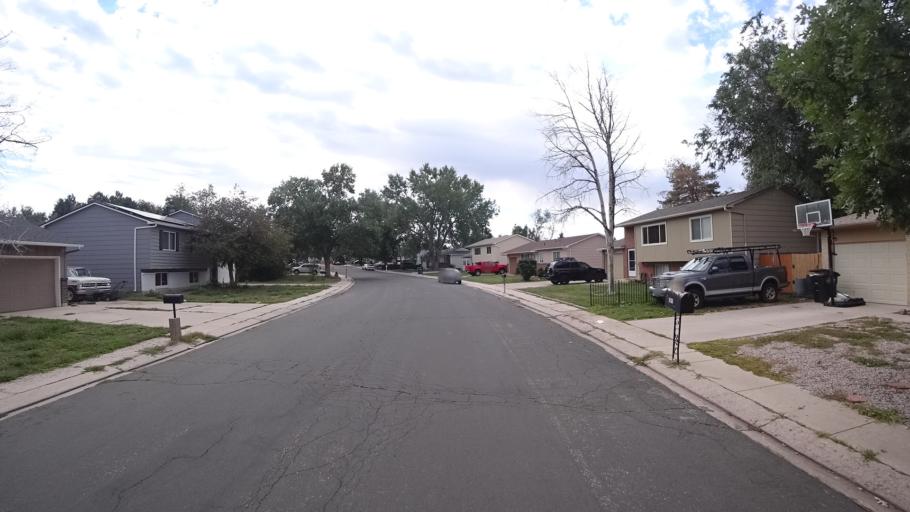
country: US
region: Colorado
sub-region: El Paso County
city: Cimarron Hills
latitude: 38.8980
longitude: -104.7542
